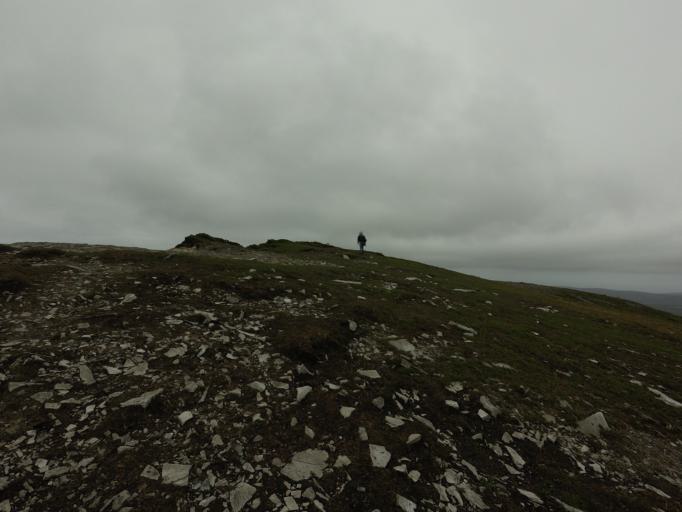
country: IE
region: Ulster
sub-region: County Donegal
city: Killybegs
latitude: 54.6471
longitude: -8.6908
